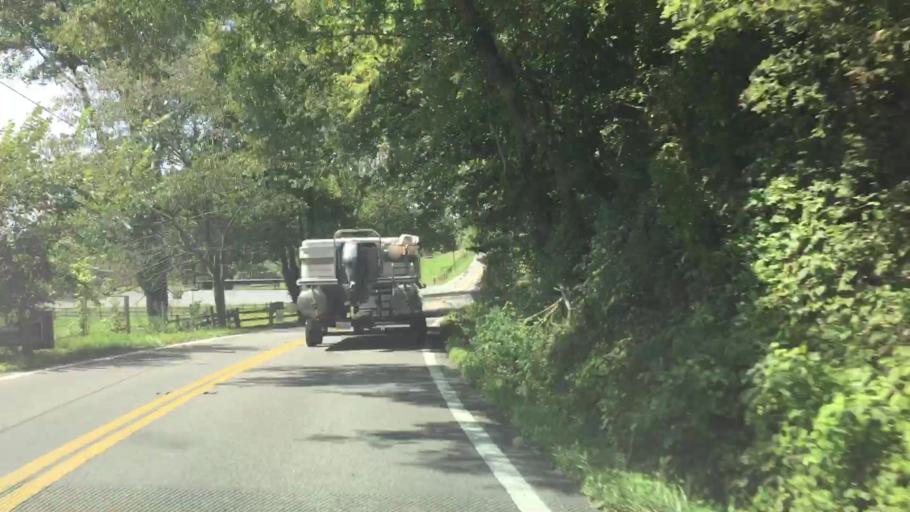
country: US
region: Virginia
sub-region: Washington County
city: Abingdon
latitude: 36.6171
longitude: -82.0178
